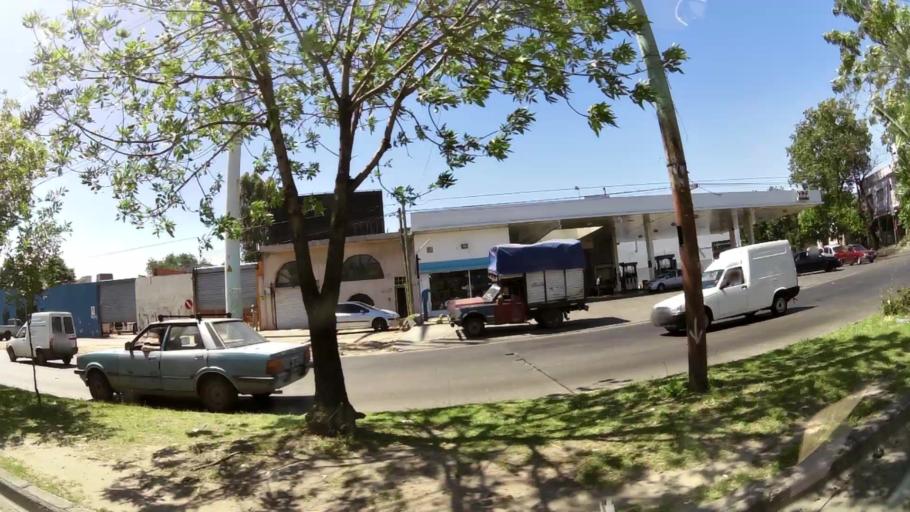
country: AR
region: Buenos Aires
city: Caseros
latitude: -34.5651
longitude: -58.5688
